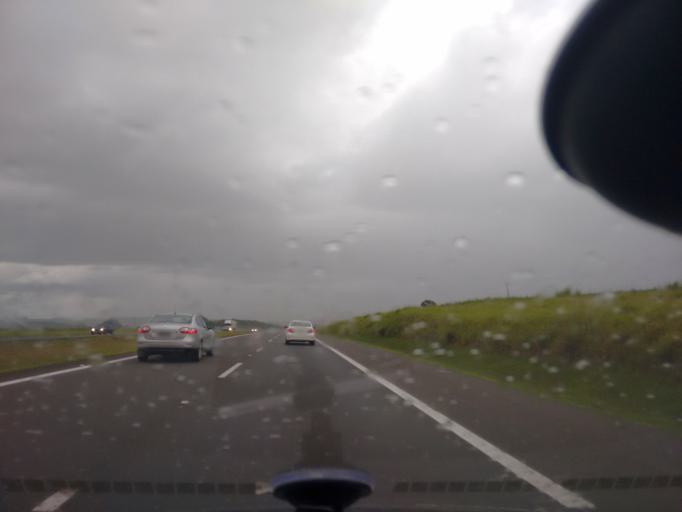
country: BR
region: Sao Paulo
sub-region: Santa Barbara D'Oeste
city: Santa Barbara d'Oeste
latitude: -22.6988
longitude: -47.4539
